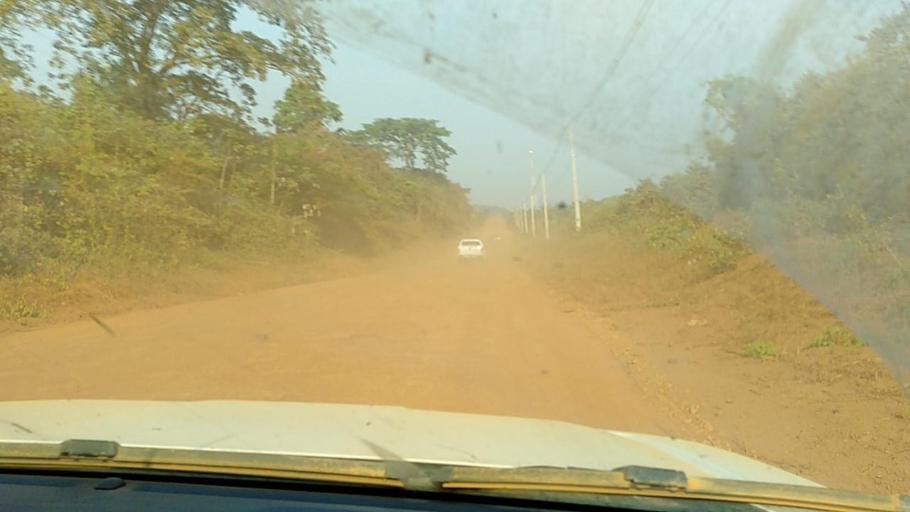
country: BR
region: Rondonia
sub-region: Porto Velho
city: Porto Velho
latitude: -8.7597
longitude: -63.9656
